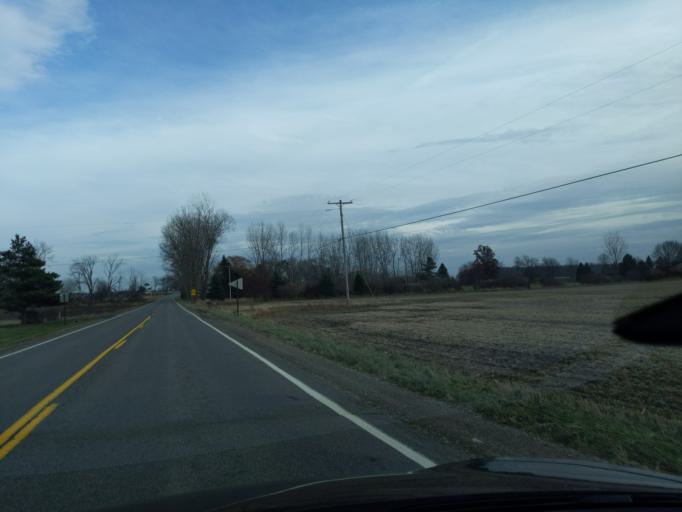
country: US
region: Michigan
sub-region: Ingham County
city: Mason
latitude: 42.6401
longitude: -84.3877
